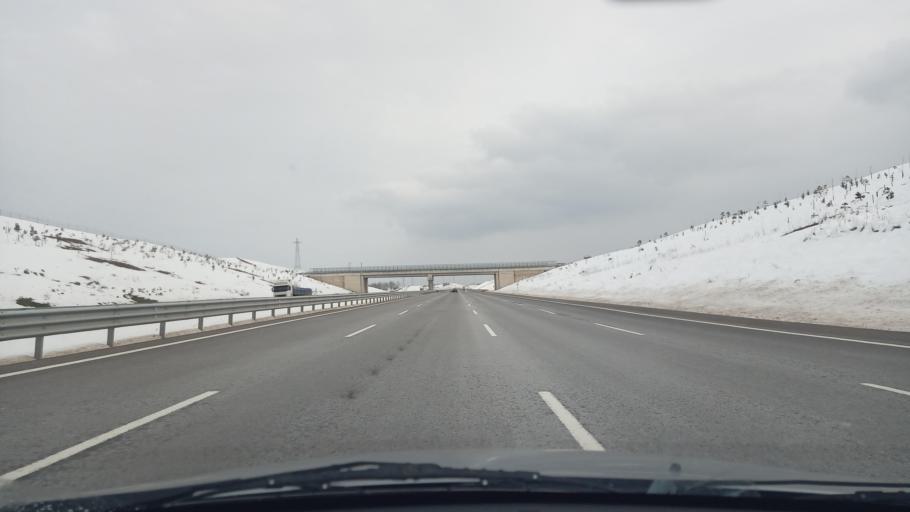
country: TR
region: Kocaeli
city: Korfez
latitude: 40.8637
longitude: 29.8271
